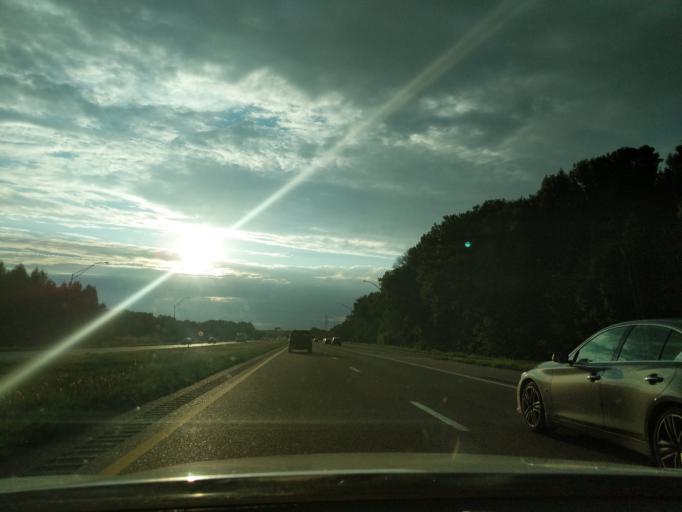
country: US
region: Tennessee
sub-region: Shelby County
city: New South Memphis
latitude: 35.0739
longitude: -90.0321
